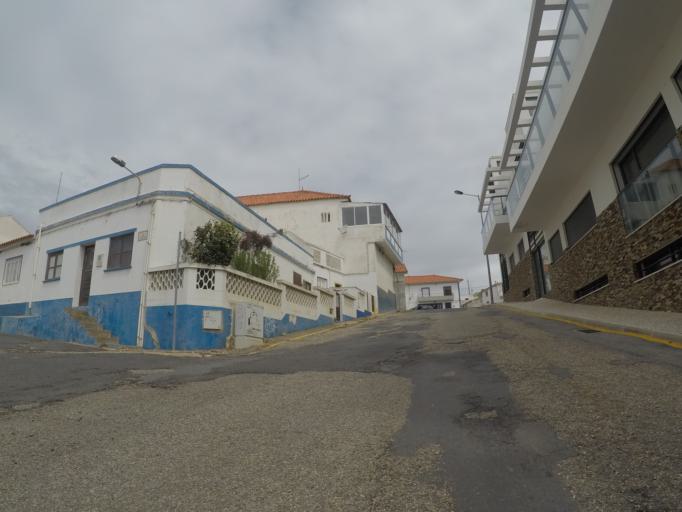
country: PT
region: Beja
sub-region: Odemira
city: Sao Teotonio
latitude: 37.5234
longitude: -8.7852
